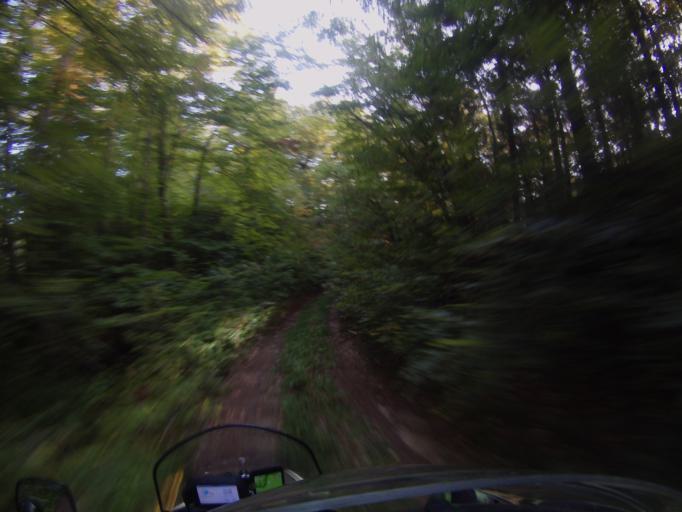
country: US
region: Vermont
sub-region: Addison County
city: Bristol
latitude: 44.0125
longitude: -72.9952
